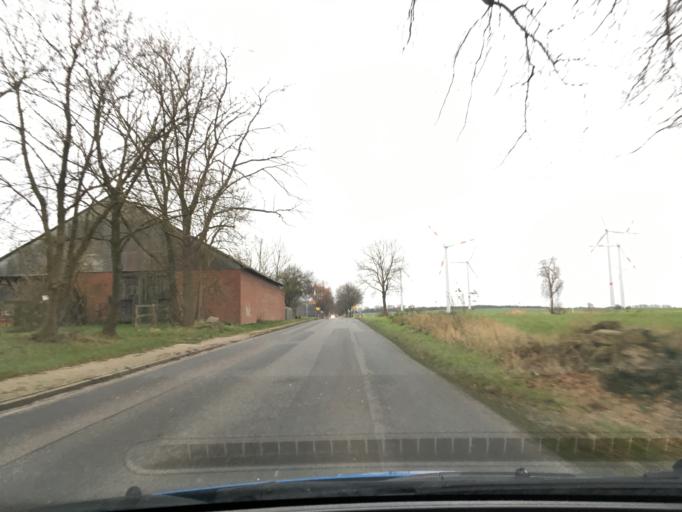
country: DE
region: Lower Saxony
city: Reinstorf
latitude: 53.2650
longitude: 10.5640
